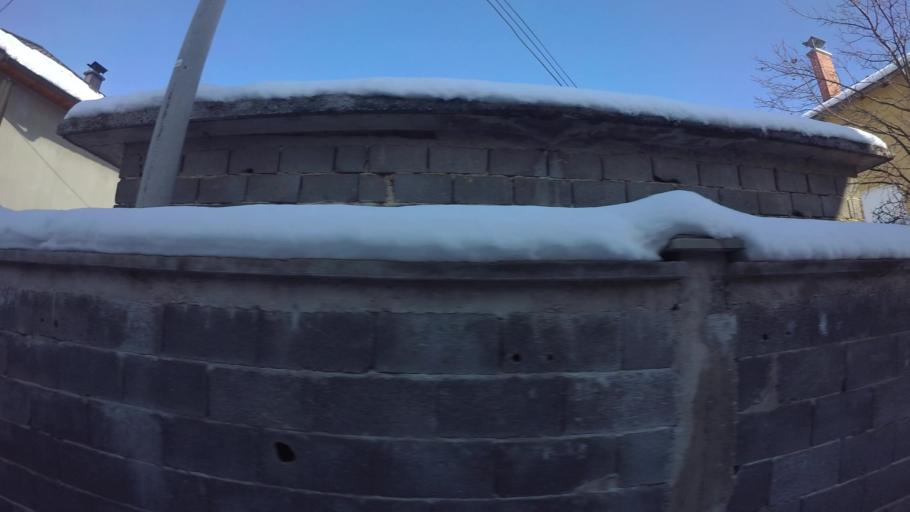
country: BA
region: Federation of Bosnia and Herzegovina
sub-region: Kanton Sarajevo
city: Sarajevo
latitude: 43.8080
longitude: 18.3159
